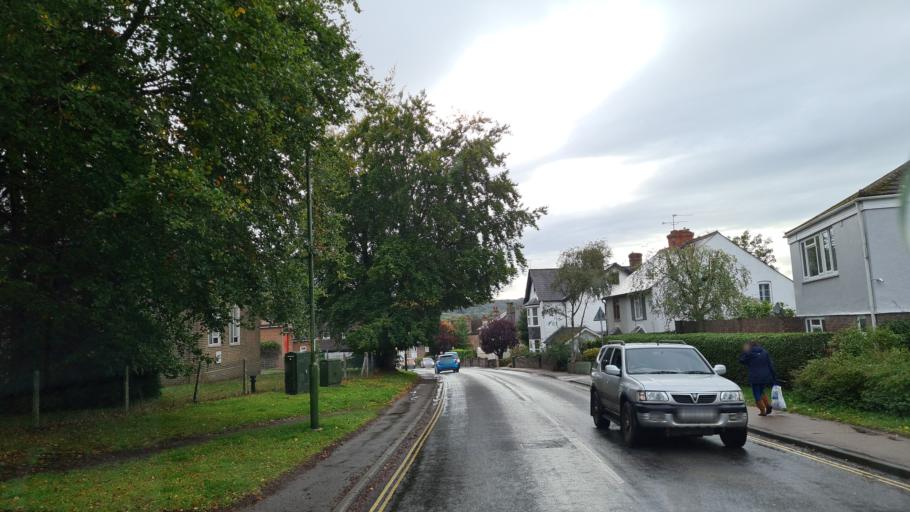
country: GB
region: England
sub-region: West Sussex
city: Storrington
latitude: 50.9198
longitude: -0.4491
